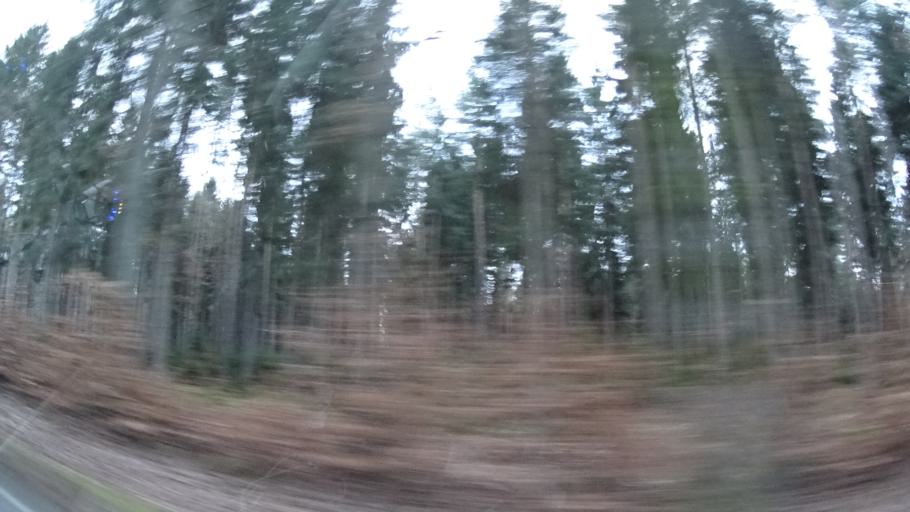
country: DE
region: Thuringia
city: Hummelshain
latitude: 50.7645
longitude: 11.6507
